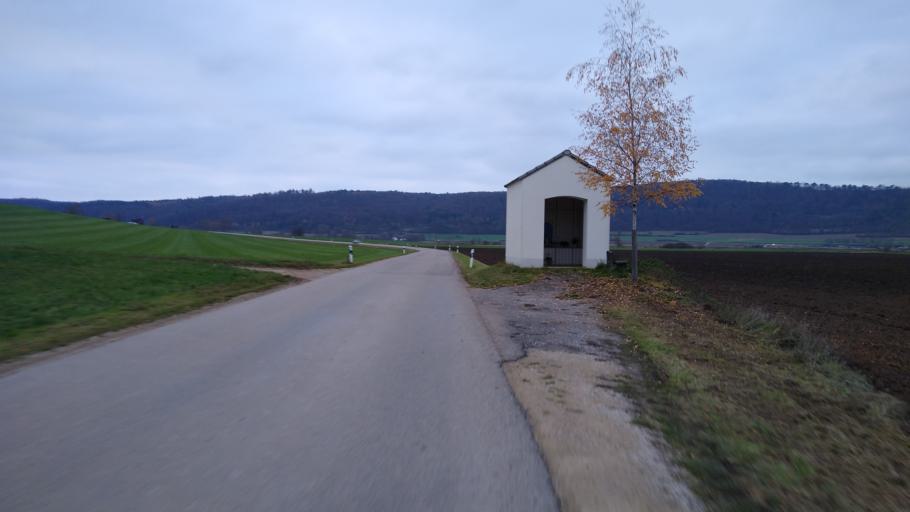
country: DE
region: Bavaria
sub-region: Upper Bavaria
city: Denkendorf
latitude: 49.0210
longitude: 11.4714
